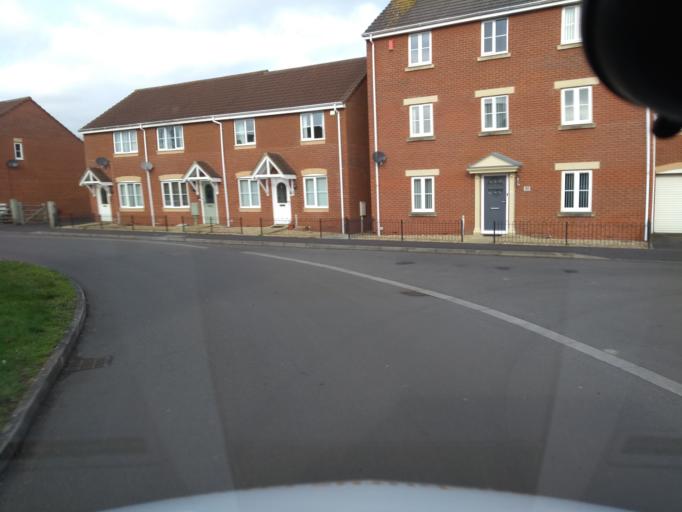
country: GB
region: England
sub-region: Somerset
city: Taunton
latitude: 51.0143
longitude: -3.0777
